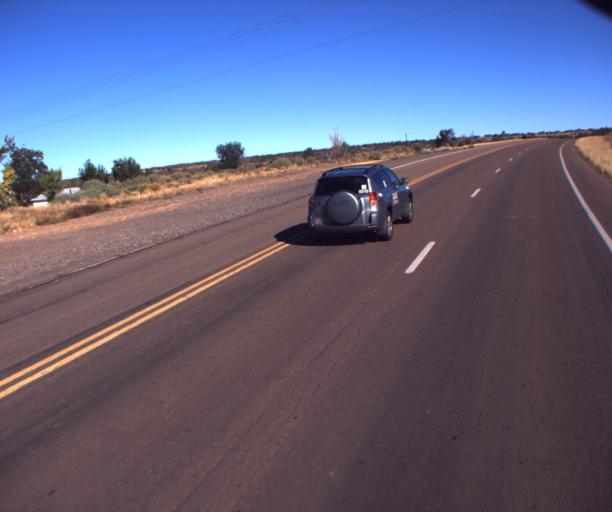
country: US
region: Arizona
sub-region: Navajo County
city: Snowflake
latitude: 34.5303
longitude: -110.0816
